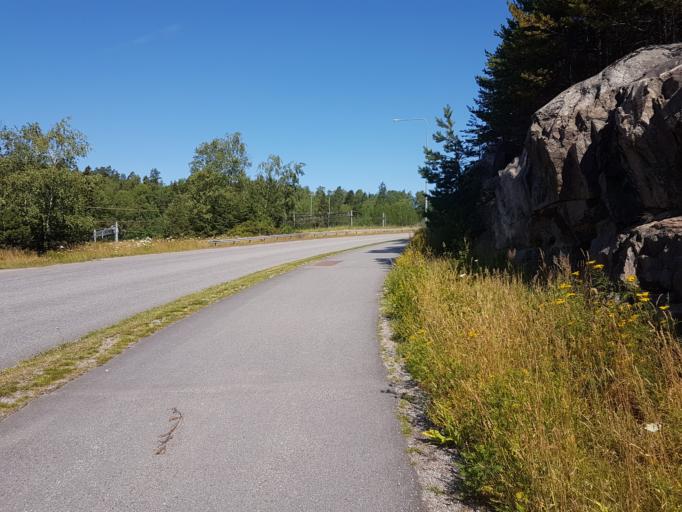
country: SE
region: Stockholm
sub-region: Huddinge Kommun
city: Huddinge
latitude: 59.2150
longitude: 17.9427
